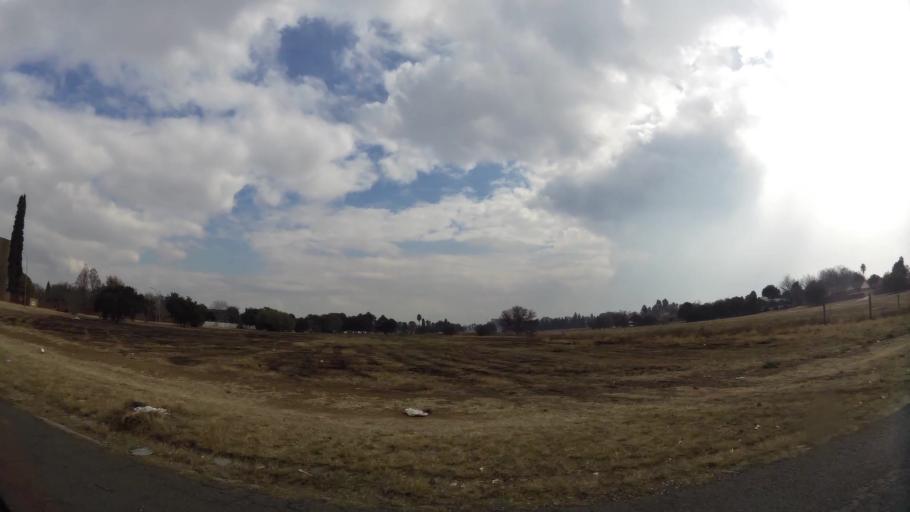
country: ZA
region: Gauteng
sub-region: Sedibeng District Municipality
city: Vanderbijlpark
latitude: -26.7138
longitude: 27.8530
